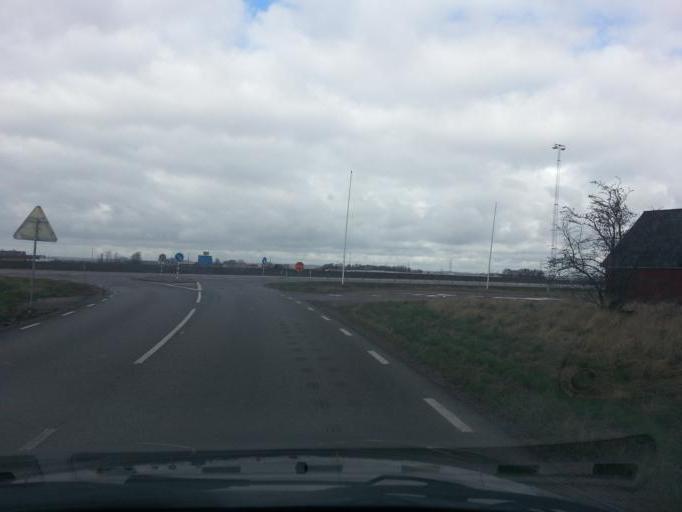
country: SE
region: Skane
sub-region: Astorps Kommun
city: Kvidinge
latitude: 56.1348
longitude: 13.0088
